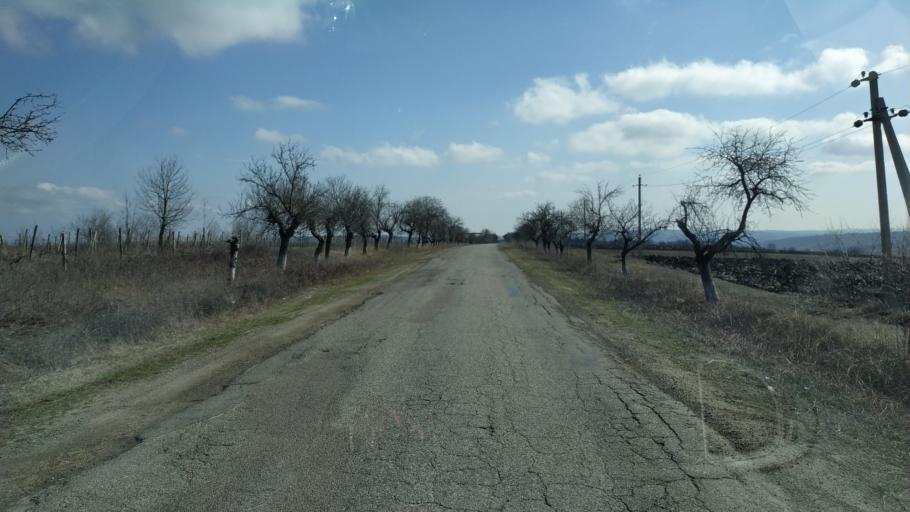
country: MD
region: Hincesti
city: Hincesti
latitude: 46.8507
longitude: 28.6486
